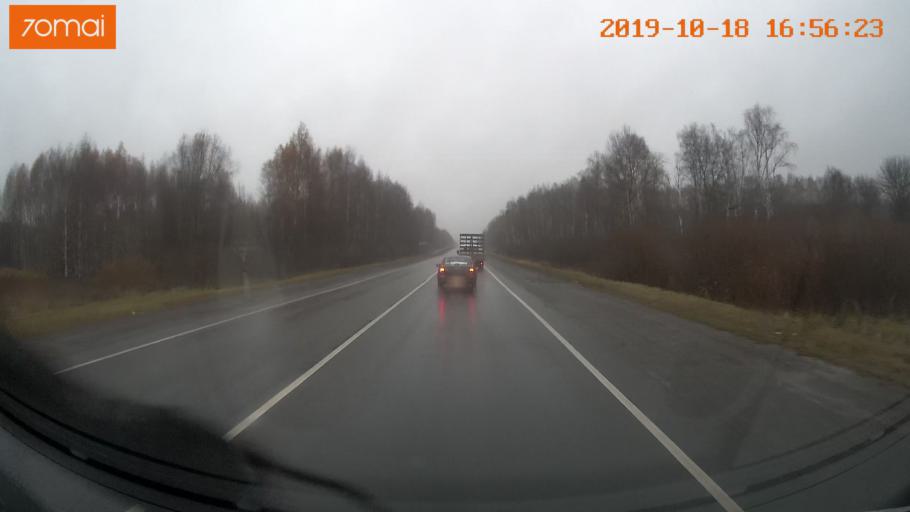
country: RU
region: Ivanovo
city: Novoye Leushino
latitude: 56.6565
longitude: 40.5879
